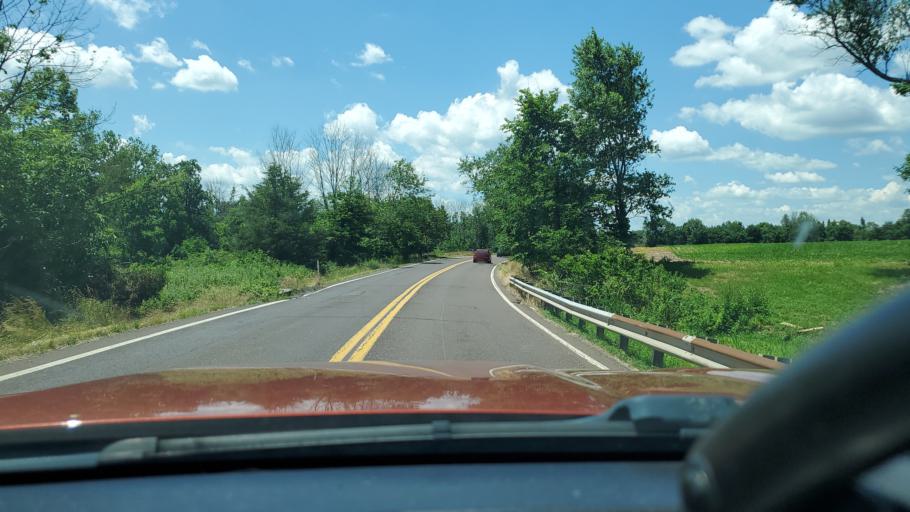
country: US
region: Pennsylvania
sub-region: Montgomery County
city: Gilbertsville
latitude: 40.3142
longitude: -75.5481
